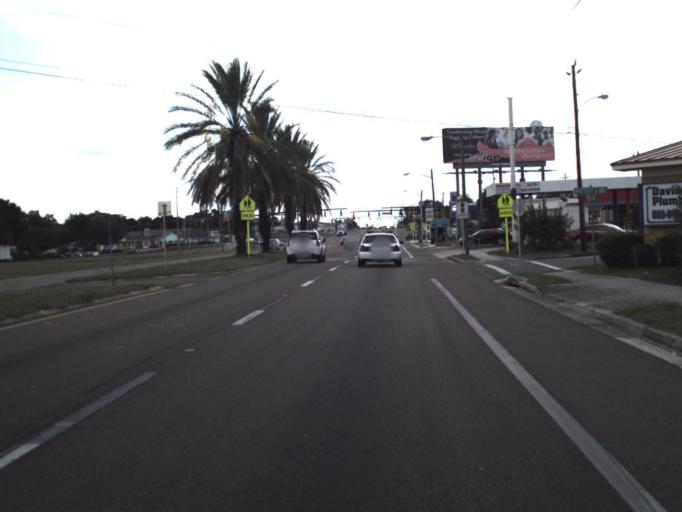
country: US
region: Florida
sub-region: Polk County
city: Crystal Lake
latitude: 28.0273
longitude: -81.9287
